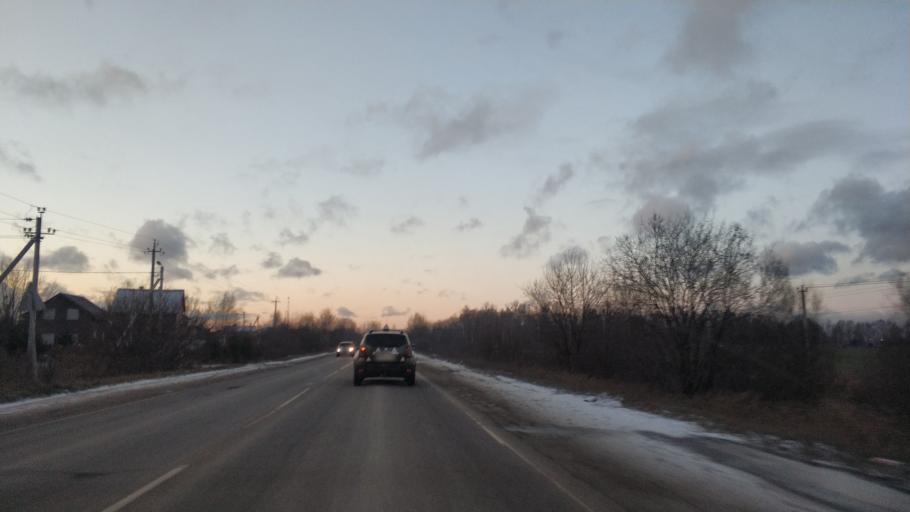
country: RU
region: St.-Petersburg
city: Pontonnyy
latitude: 59.8043
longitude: 30.6271
